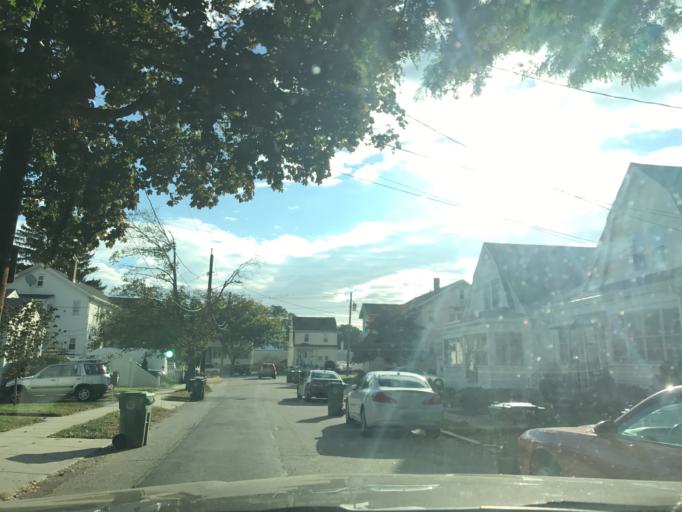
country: US
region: Massachusetts
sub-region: Middlesex County
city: Watertown
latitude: 42.3703
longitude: -71.1570
